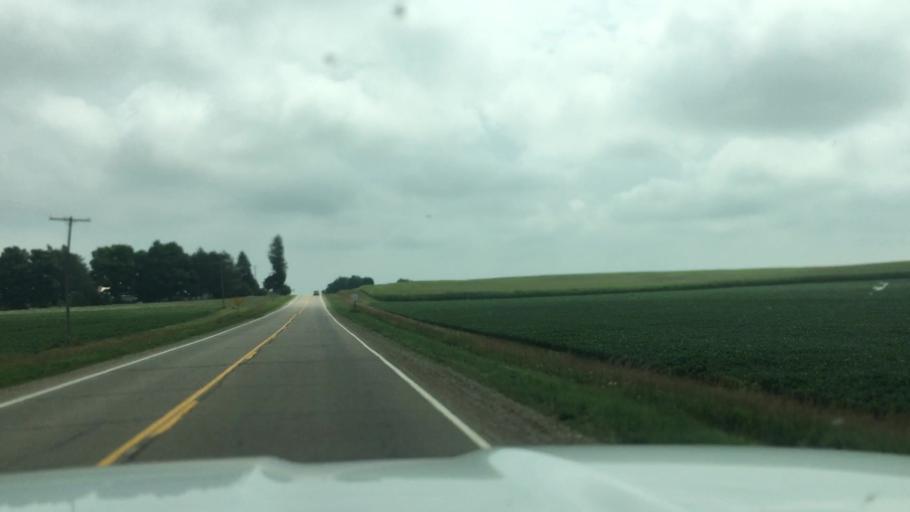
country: US
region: Michigan
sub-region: Sanilac County
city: Marlette
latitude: 43.3299
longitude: -82.9821
